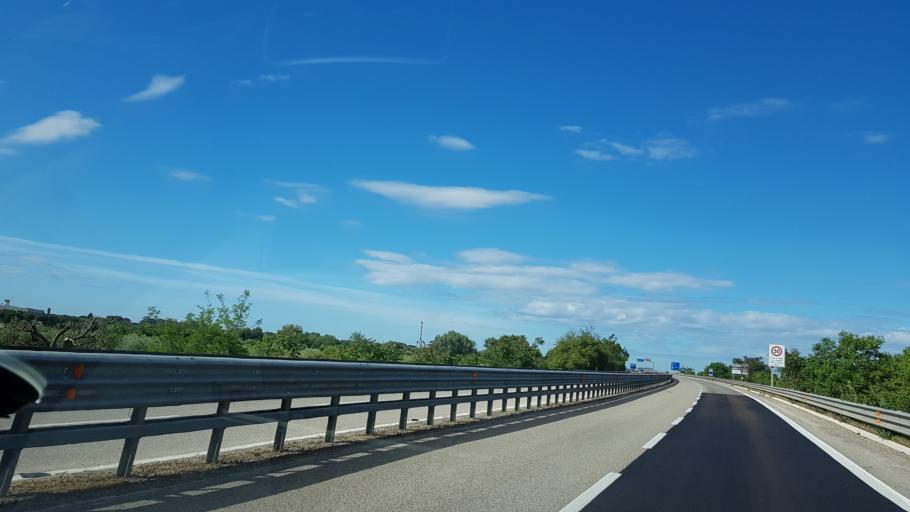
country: IT
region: Apulia
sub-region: Provincia di Brindisi
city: Francavilla Fontana
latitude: 40.5424
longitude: 17.5363
